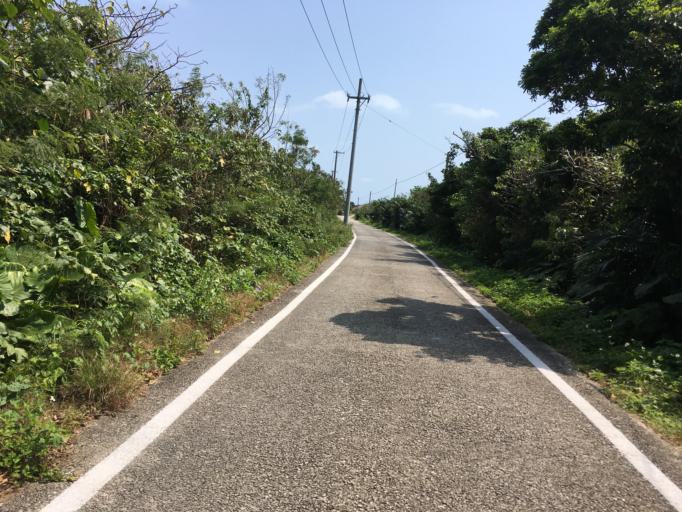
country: JP
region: Okinawa
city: Ishigaki
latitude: 24.3252
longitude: 124.0819
